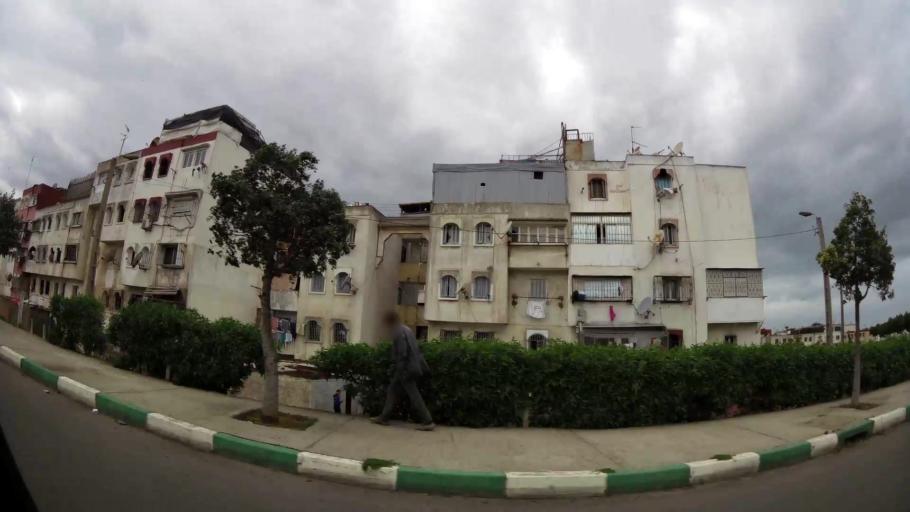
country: MA
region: Grand Casablanca
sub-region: Casablanca
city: Casablanca
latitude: 33.5910
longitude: -7.5521
